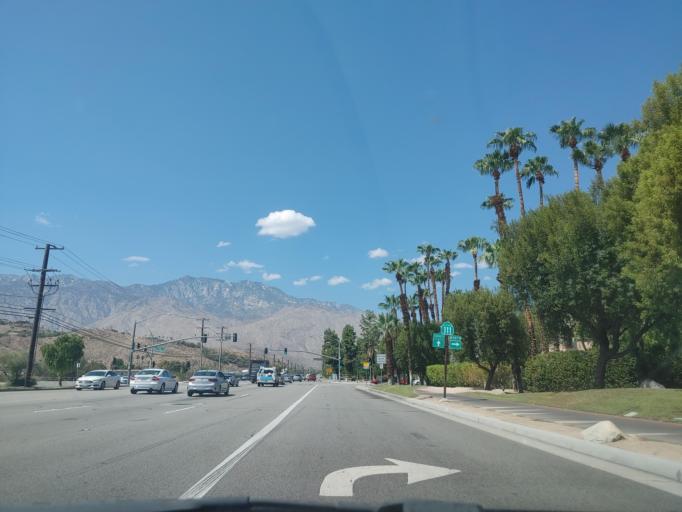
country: US
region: California
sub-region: Riverside County
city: Cathedral City
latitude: 33.7932
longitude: -116.4942
